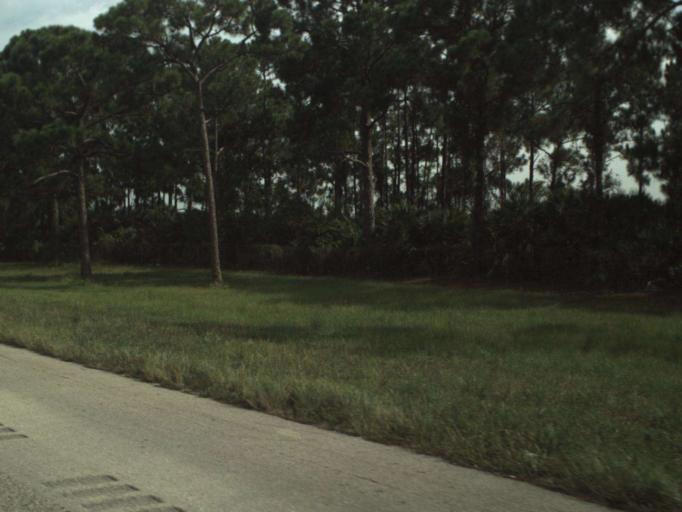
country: US
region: Florida
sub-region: Saint Lucie County
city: Port Saint Lucie
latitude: 27.2358
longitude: -80.4096
